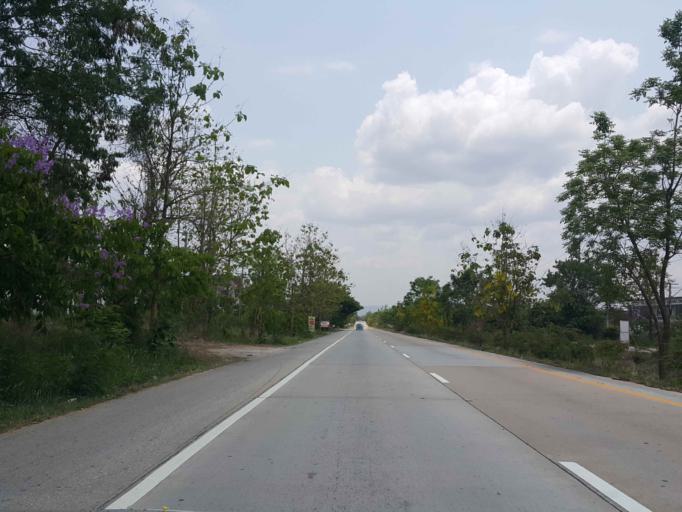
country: TH
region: Lampang
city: Hang Chat
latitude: 18.3017
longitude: 99.4056
